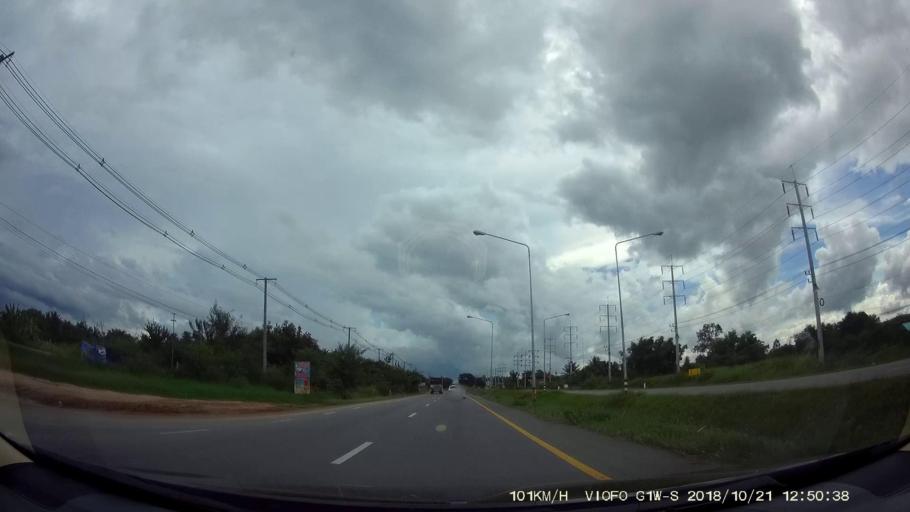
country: TH
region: Nakhon Ratchasima
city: Amphoe Sikhiu
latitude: 14.8794
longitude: 101.6913
